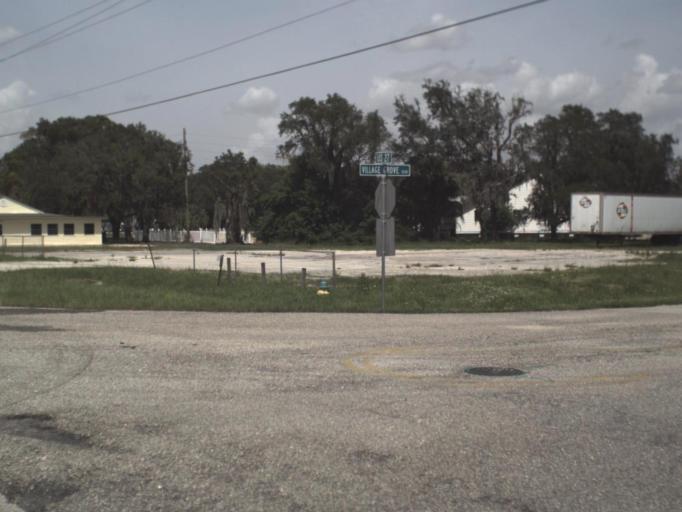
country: US
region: Florida
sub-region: Highlands County
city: Sebring
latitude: 27.4627
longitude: -81.4320
